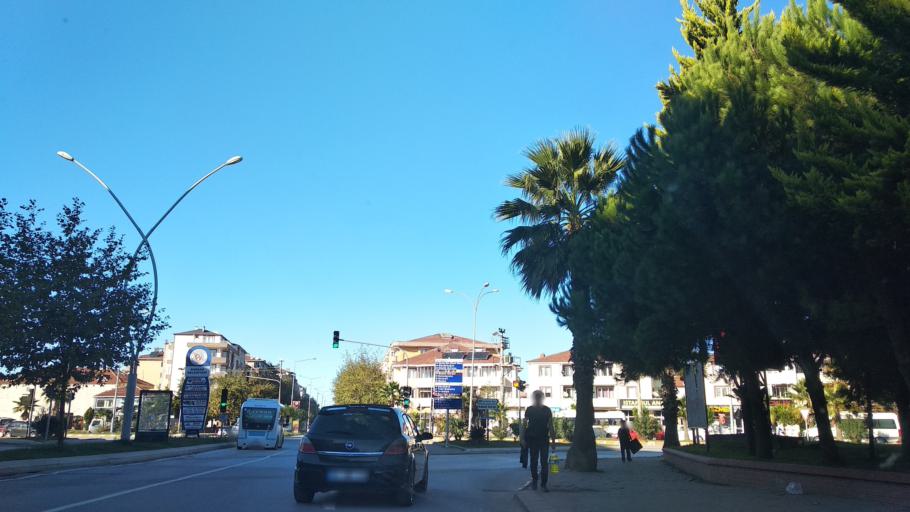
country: TR
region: Sakarya
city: Karasu
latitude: 41.1045
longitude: 30.6927
